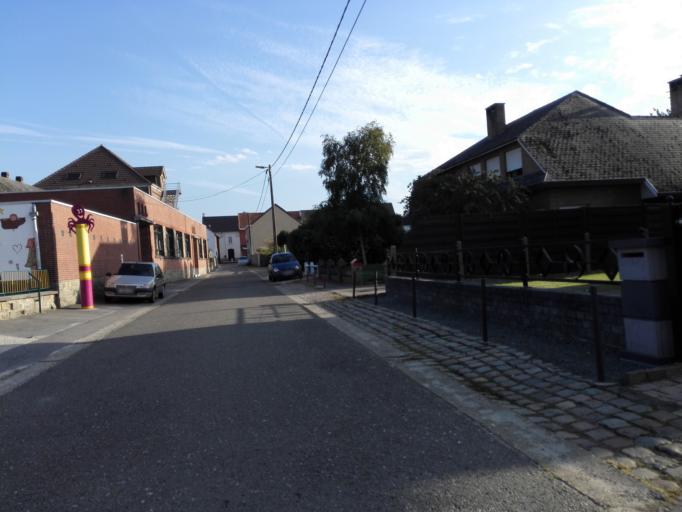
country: BE
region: Flanders
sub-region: Provincie Vlaams-Brabant
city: Oud-Heverlee
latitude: 50.8040
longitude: 4.6490
